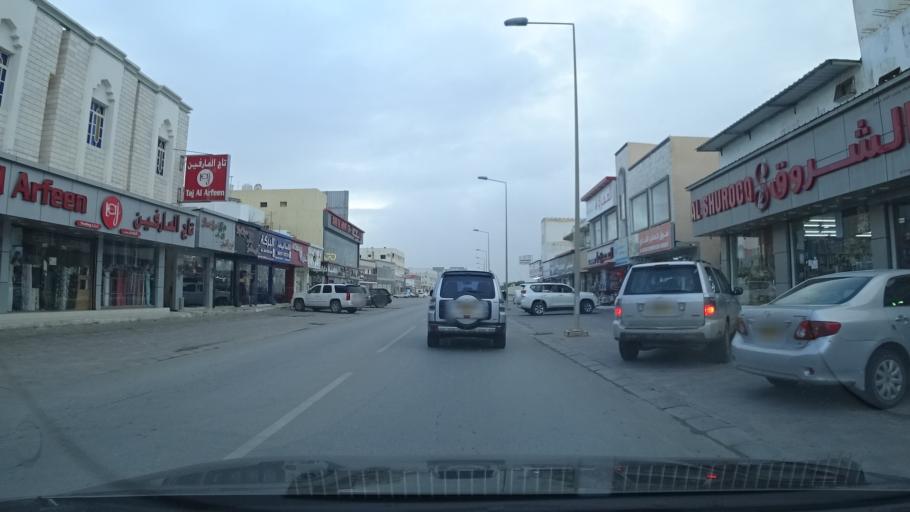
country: OM
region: Zufar
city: Salalah
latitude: 17.0092
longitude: 54.0791
